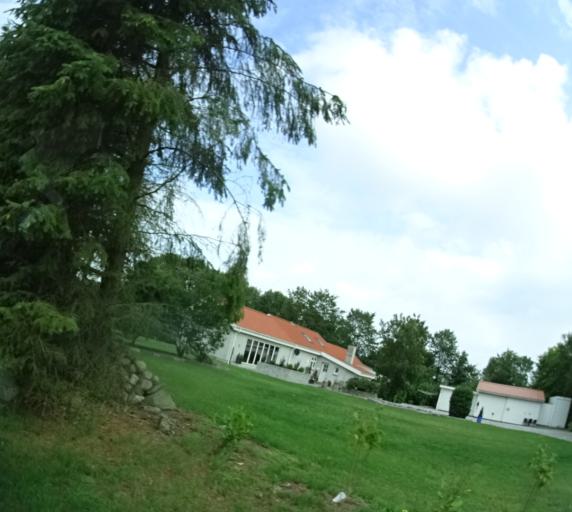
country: DK
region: Central Jutland
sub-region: Syddjurs Kommune
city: Ryomgard
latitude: 56.3697
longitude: 10.4985
